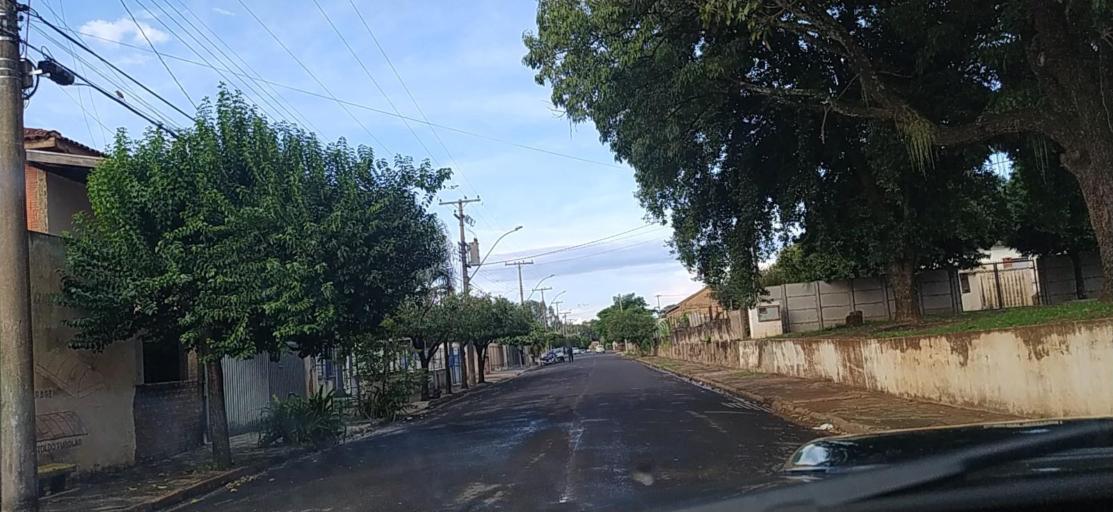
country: BR
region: Sao Paulo
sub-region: Pindorama
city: Pindorama
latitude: -21.1873
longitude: -48.9034
